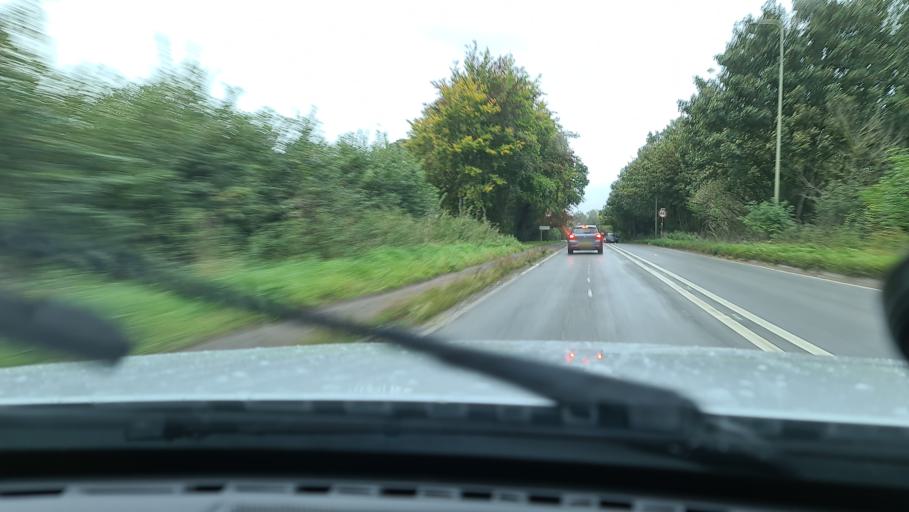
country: GB
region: England
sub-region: Oxfordshire
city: Adderbury
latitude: 52.0326
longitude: -1.3165
